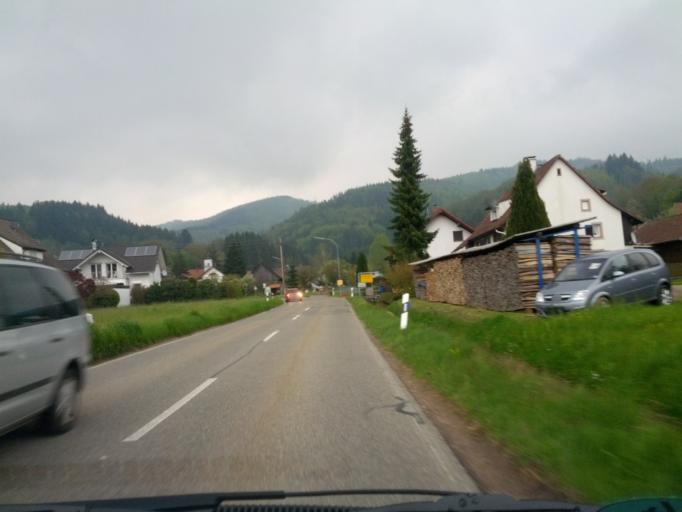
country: DE
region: Baden-Wuerttemberg
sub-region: Freiburg Region
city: Schopfheim
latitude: 47.6786
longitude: 7.8073
